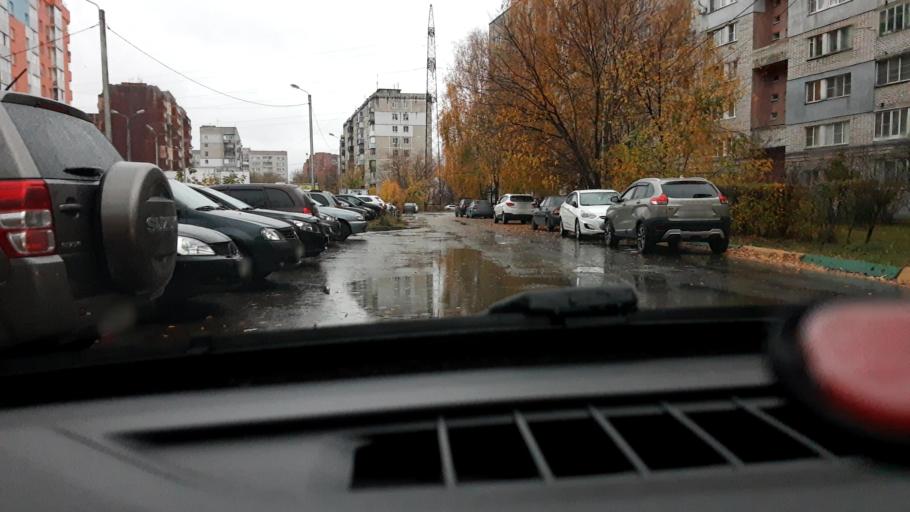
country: RU
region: Nizjnij Novgorod
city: Gorbatovka
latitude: 56.2912
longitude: 43.8411
